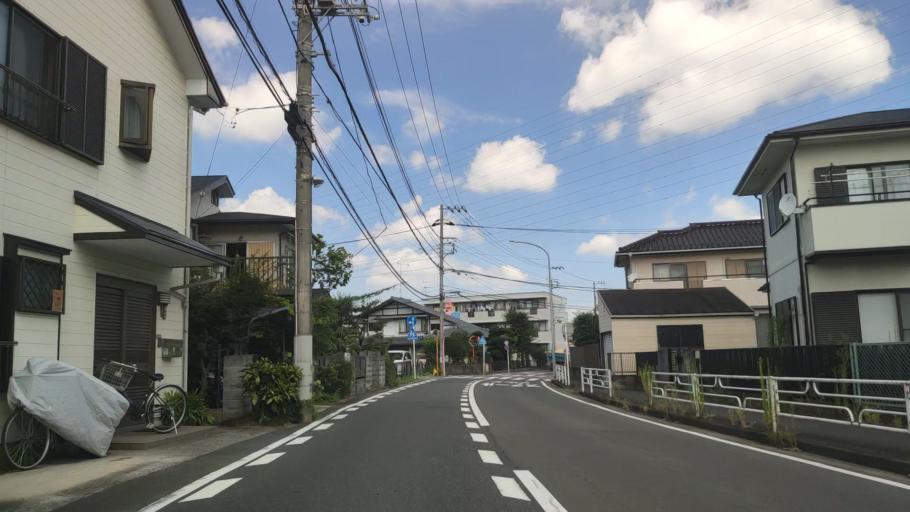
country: JP
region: Kanagawa
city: Yokohama
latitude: 35.5316
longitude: 139.6201
